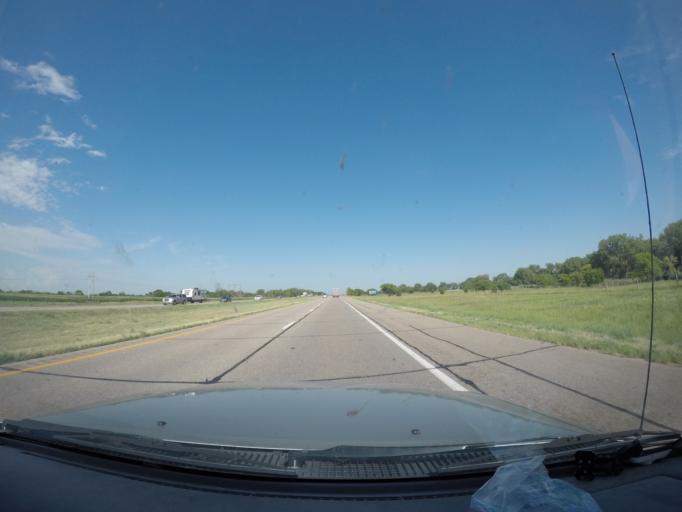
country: US
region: Nebraska
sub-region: Phelps County
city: Holdrege
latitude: 40.6907
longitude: -99.3565
